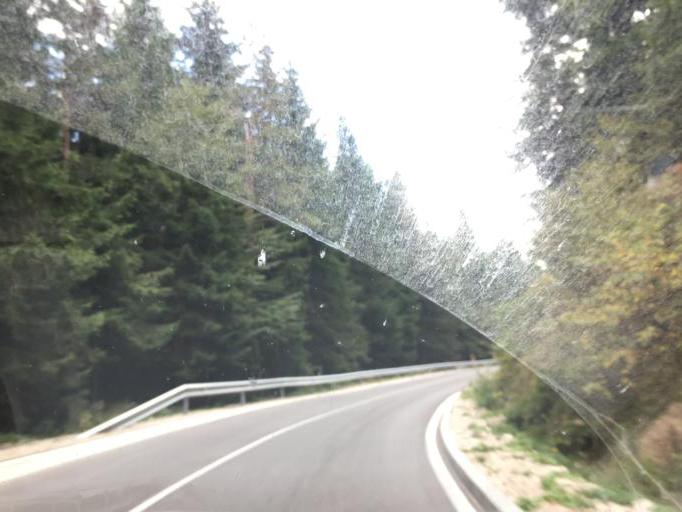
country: BG
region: Pazardzhik
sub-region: Obshtina Batak
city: Batak
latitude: 41.9033
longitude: 24.3026
